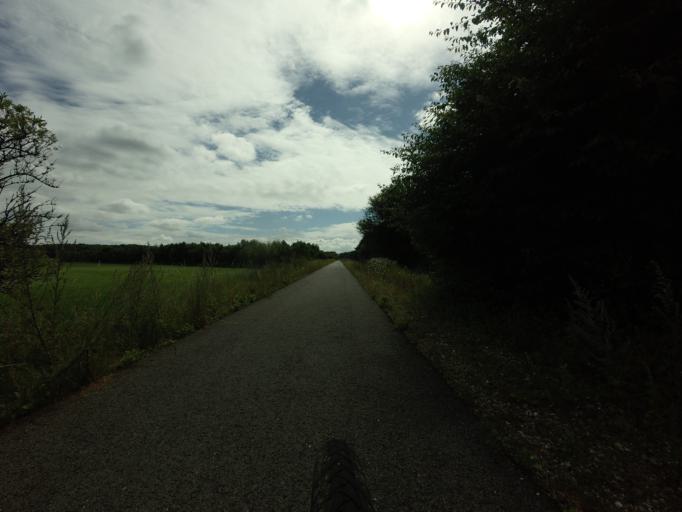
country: DK
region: Central Jutland
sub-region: Norddjurs Kommune
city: Auning
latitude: 56.4152
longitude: 10.3901
